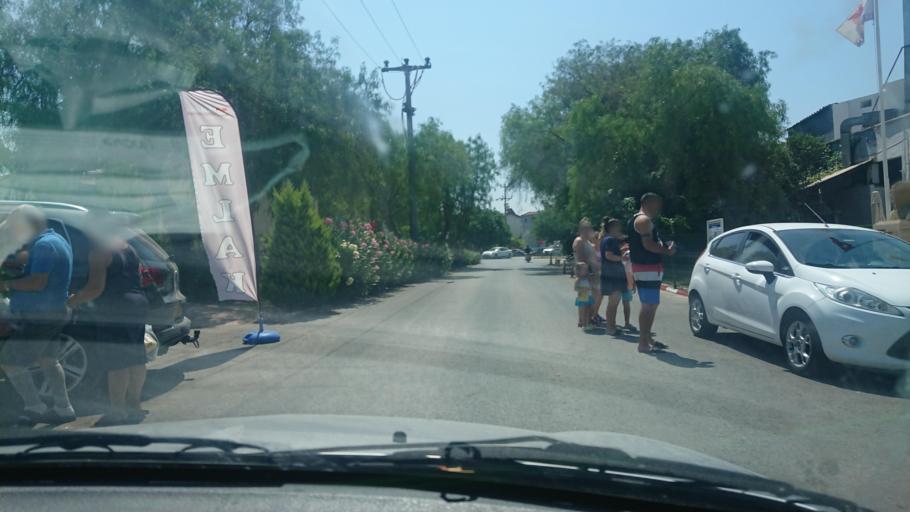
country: TR
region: Aydin
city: Kusadasi
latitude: 37.7991
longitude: 27.2732
